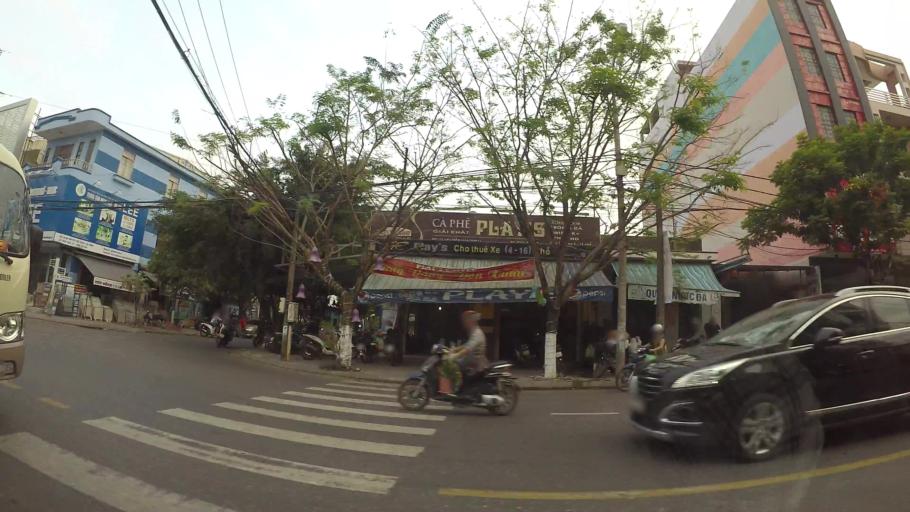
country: VN
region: Da Nang
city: Son Tra
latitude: 16.0541
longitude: 108.2390
